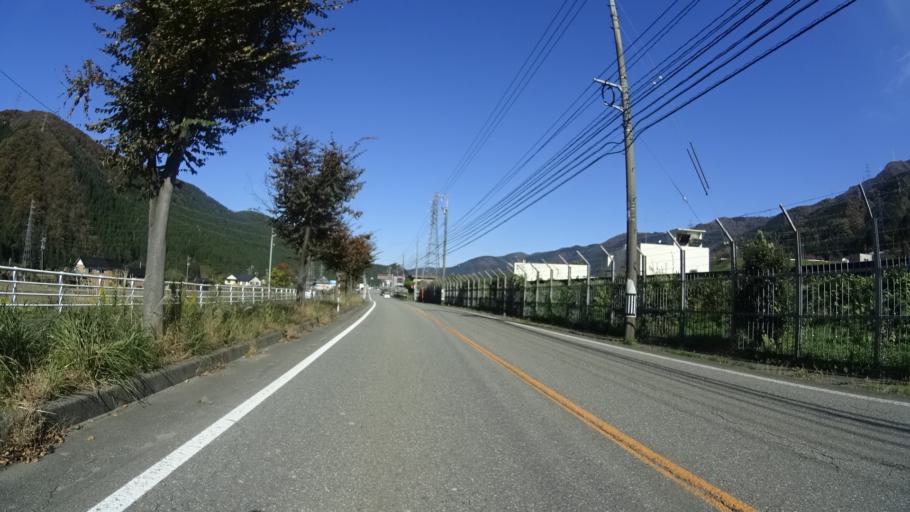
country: JP
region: Ishikawa
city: Tsurugi-asahimachi
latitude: 36.4161
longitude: 136.6322
